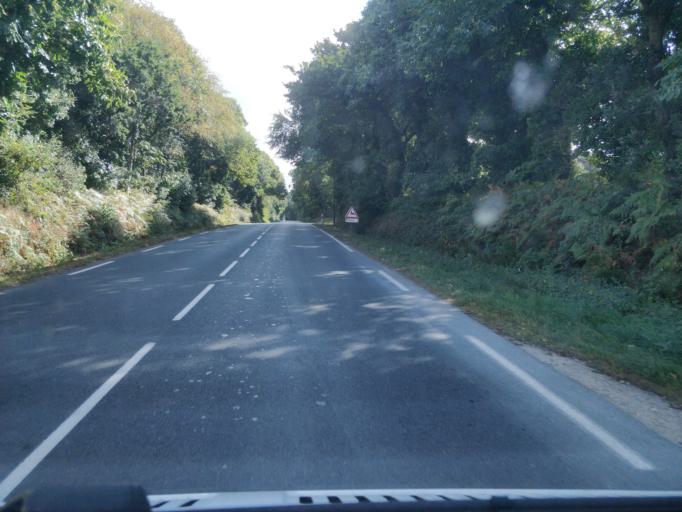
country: FR
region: Brittany
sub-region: Departement du Finistere
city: Landudec
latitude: 47.9987
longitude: -4.3173
